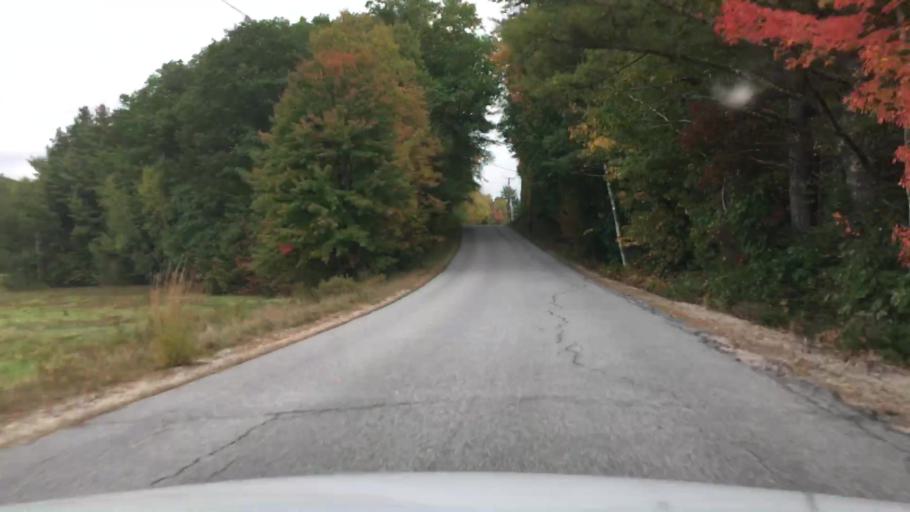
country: US
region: Maine
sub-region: Cumberland County
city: Harrison
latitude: 44.2528
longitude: -70.7230
